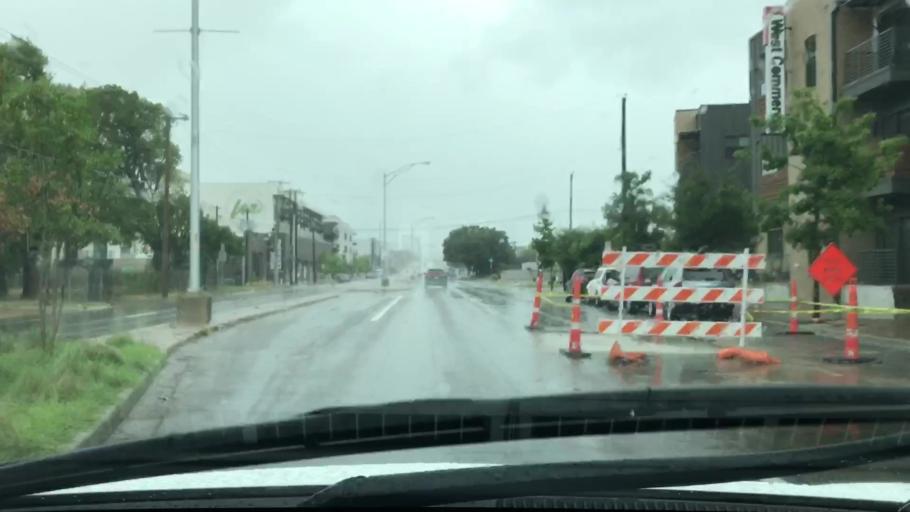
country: US
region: Texas
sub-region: Dallas County
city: Dallas
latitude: 32.7733
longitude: -96.8301
